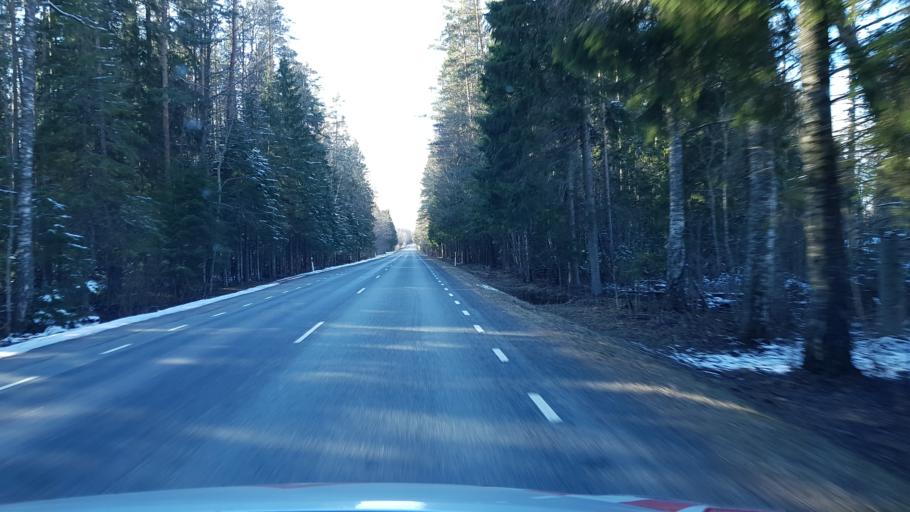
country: EE
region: Laeaene-Virumaa
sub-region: Tapa vald
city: Tapa
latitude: 59.4304
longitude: 25.9740
